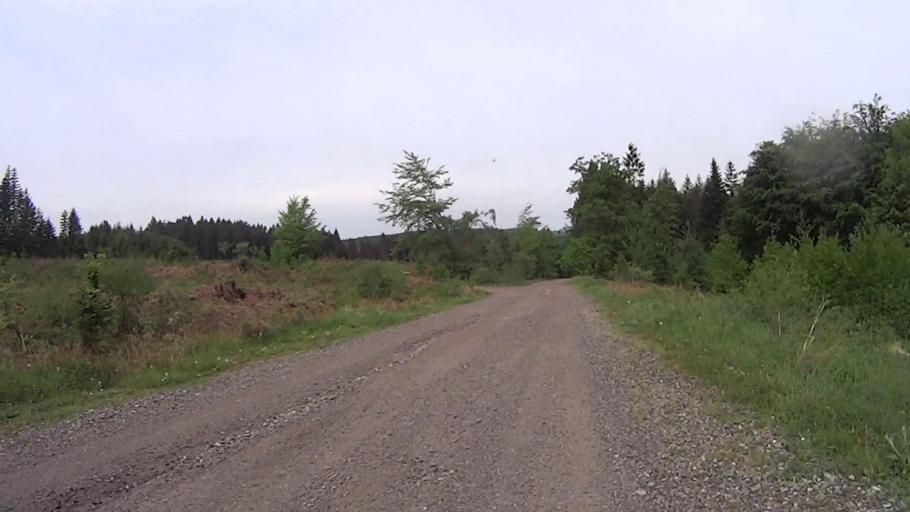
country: BE
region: Wallonia
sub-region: Province de Liege
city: Malmedy
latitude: 50.4404
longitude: 5.9842
